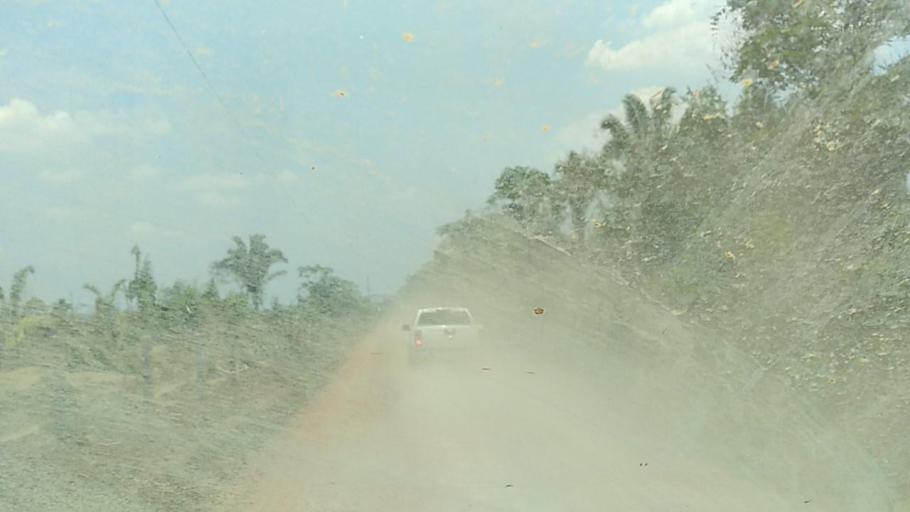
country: BR
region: Rondonia
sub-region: Porto Velho
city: Porto Velho
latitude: -8.7228
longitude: -63.3103
